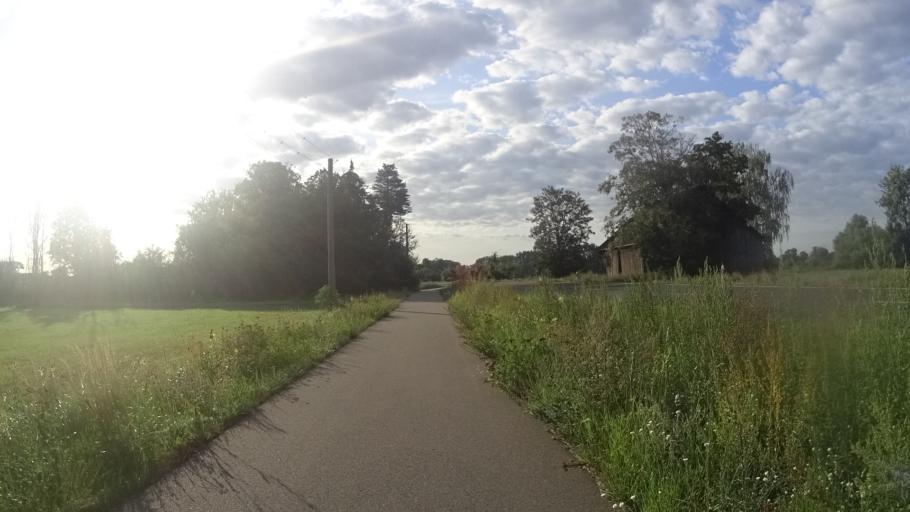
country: DE
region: Brandenburg
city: Premnitz
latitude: 52.5039
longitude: 12.4446
